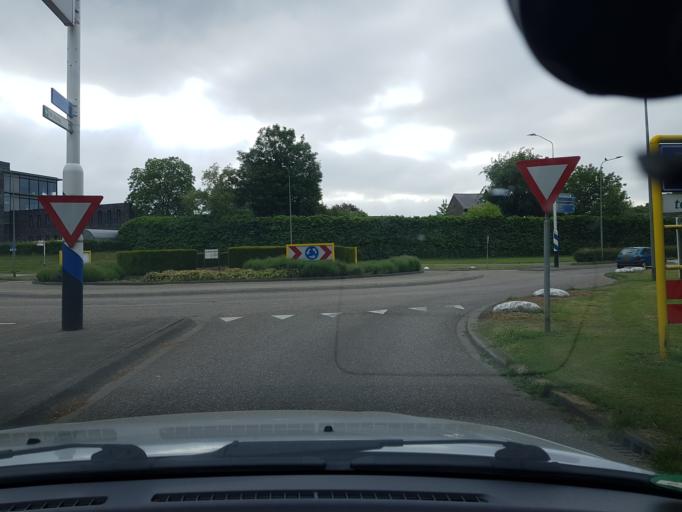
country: NL
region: Limburg
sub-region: Gemeente Stein
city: Elsloo
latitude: 50.9480
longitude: 5.7825
